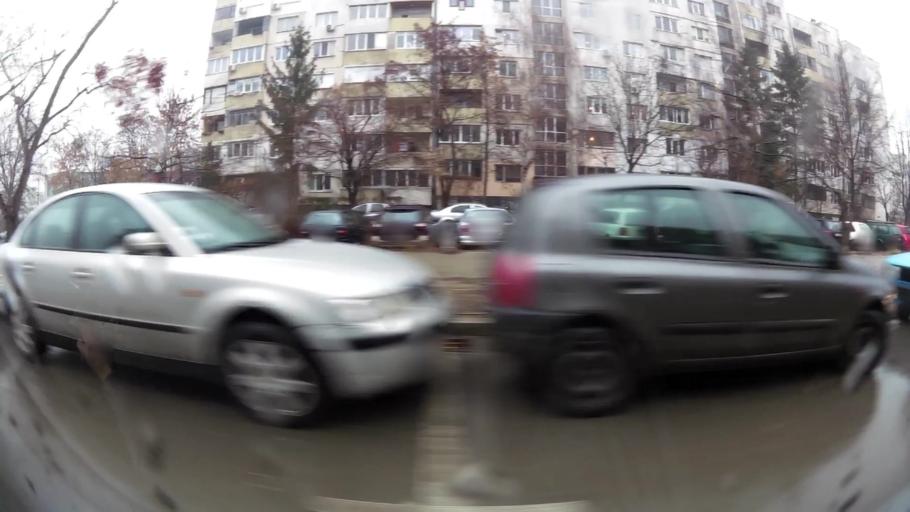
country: BG
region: Sofia-Capital
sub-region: Stolichna Obshtina
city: Sofia
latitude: 42.6536
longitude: 23.3955
